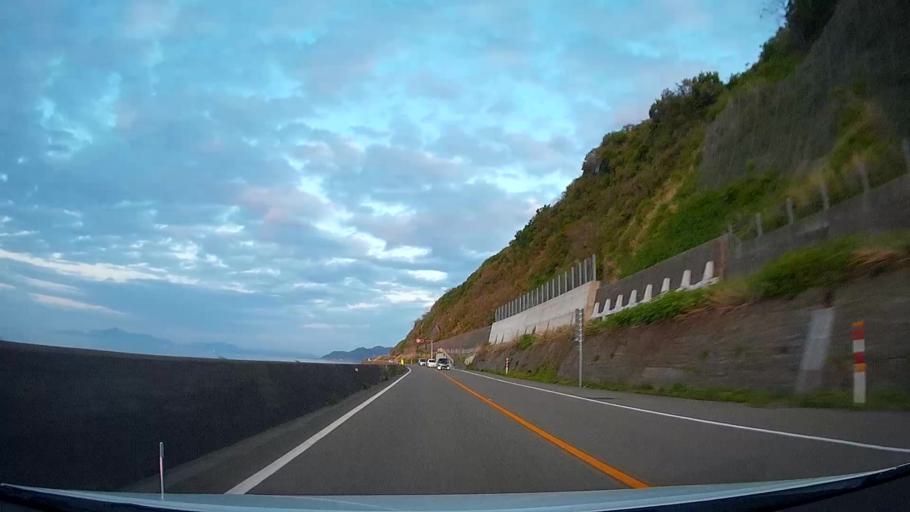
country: JP
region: Niigata
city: Joetsu
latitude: 37.1729
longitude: 138.1049
